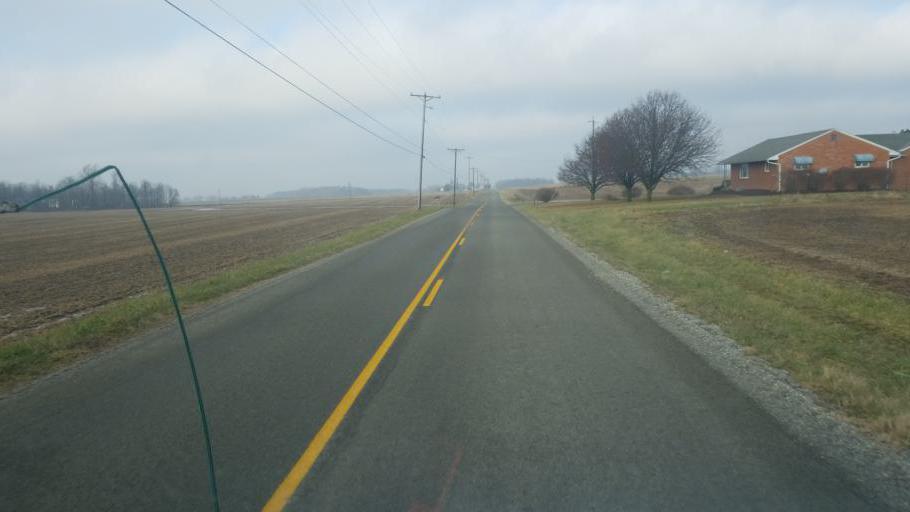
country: US
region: Ohio
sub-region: Hardin County
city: Kenton
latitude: 40.6692
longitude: -83.5761
